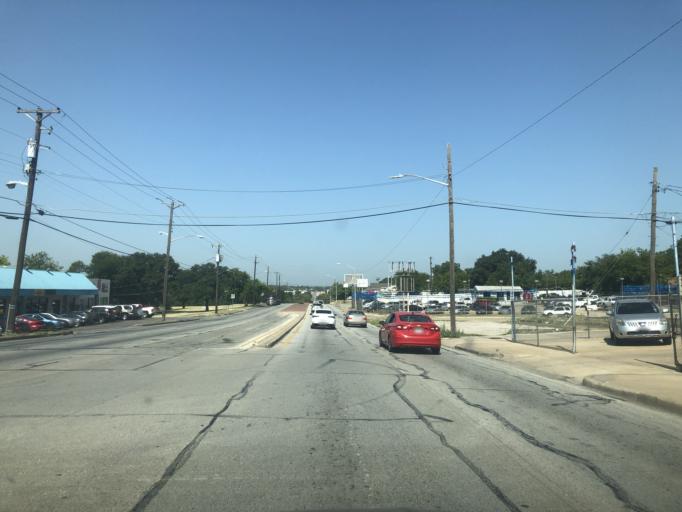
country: US
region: Texas
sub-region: Tarrant County
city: Blue Mound
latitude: 32.7953
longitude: -97.3316
